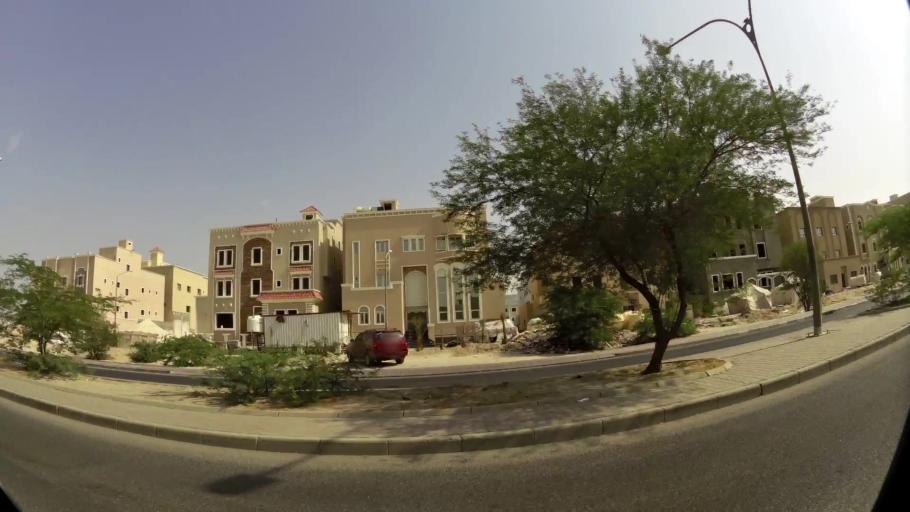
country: KW
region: Muhafazat al Jahra'
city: Al Jahra'
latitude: 29.3225
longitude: 47.6795
